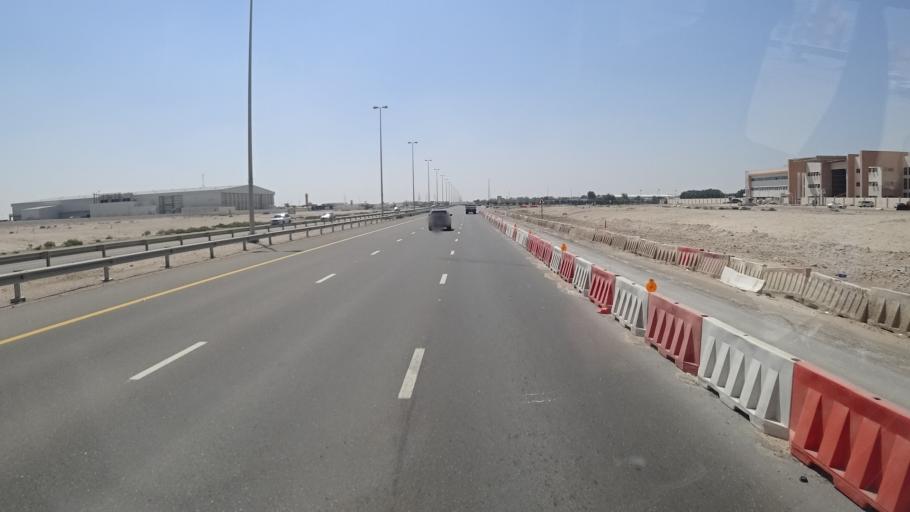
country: AE
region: Abu Dhabi
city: Abu Dhabi
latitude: 24.3123
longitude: 54.6764
